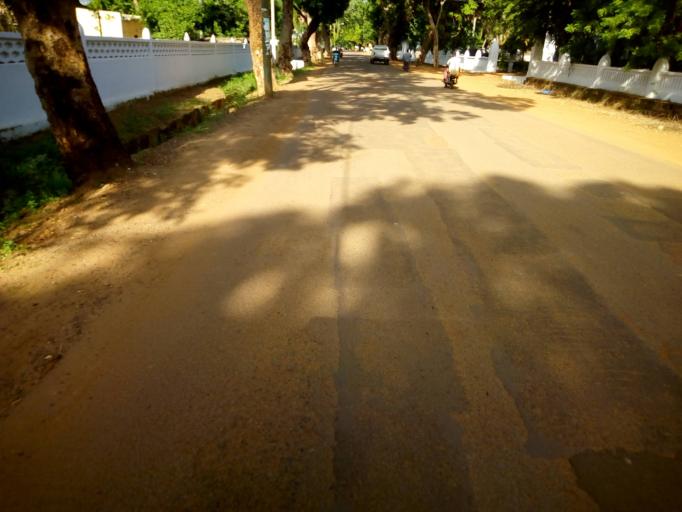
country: ML
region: Segou
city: Segou
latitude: 13.4393
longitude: -6.2812
